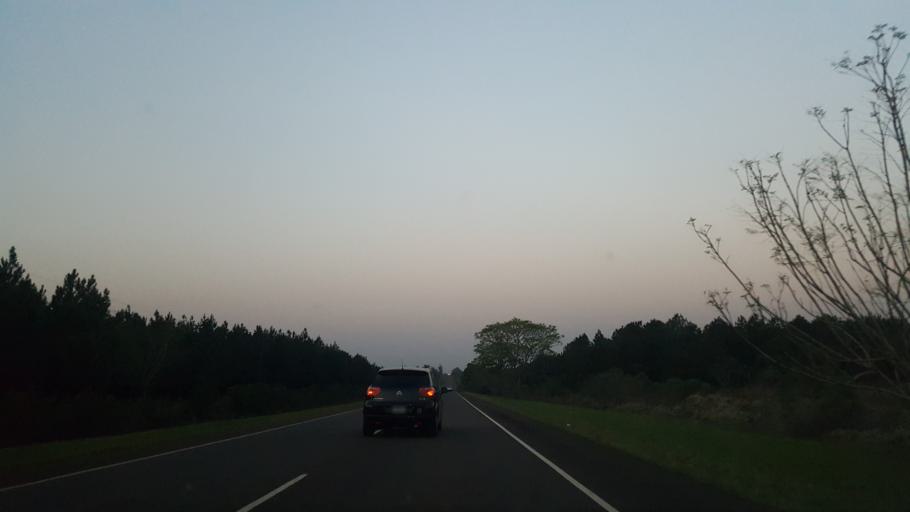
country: AR
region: Misiones
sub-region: Departamento de Capital
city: Posadas
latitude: -27.4343
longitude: -56.0119
